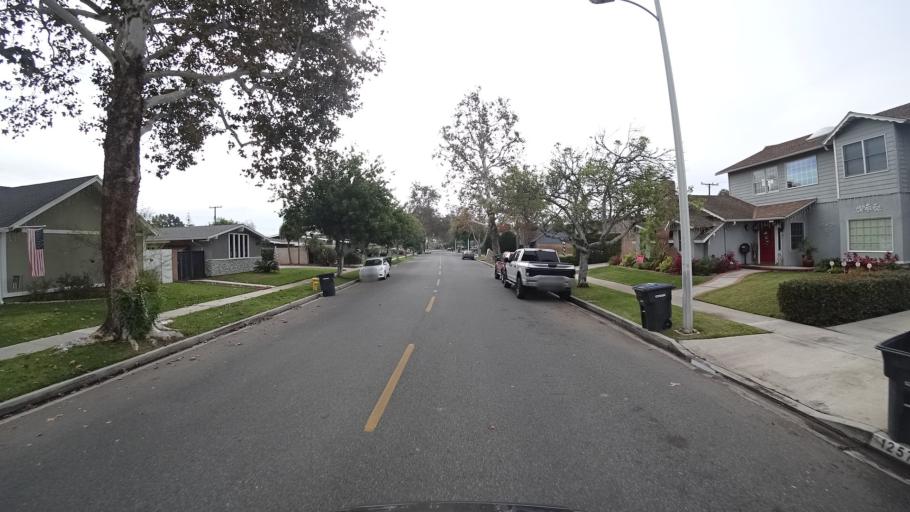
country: US
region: California
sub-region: Orange County
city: Rossmoor
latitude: 33.7805
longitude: -118.0890
